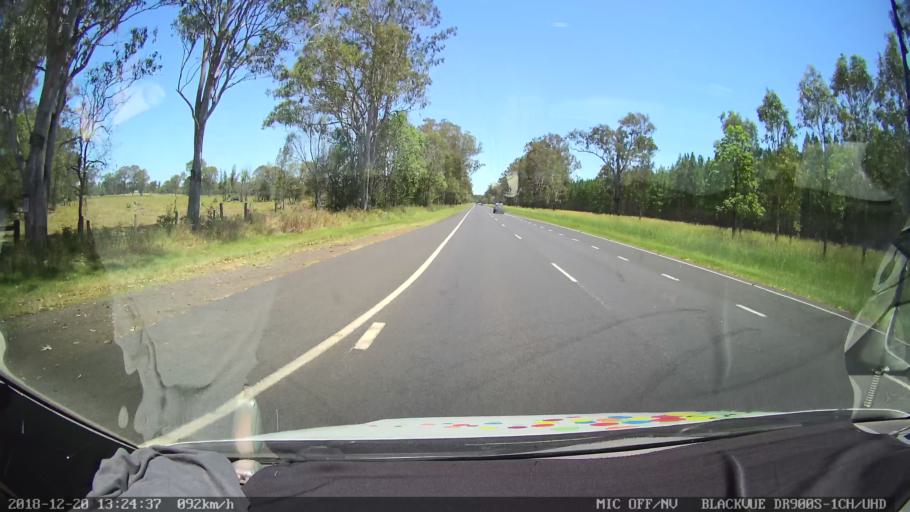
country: AU
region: New South Wales
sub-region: Richmond Valley
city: Casino
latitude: -29.1200
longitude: 152.9996
